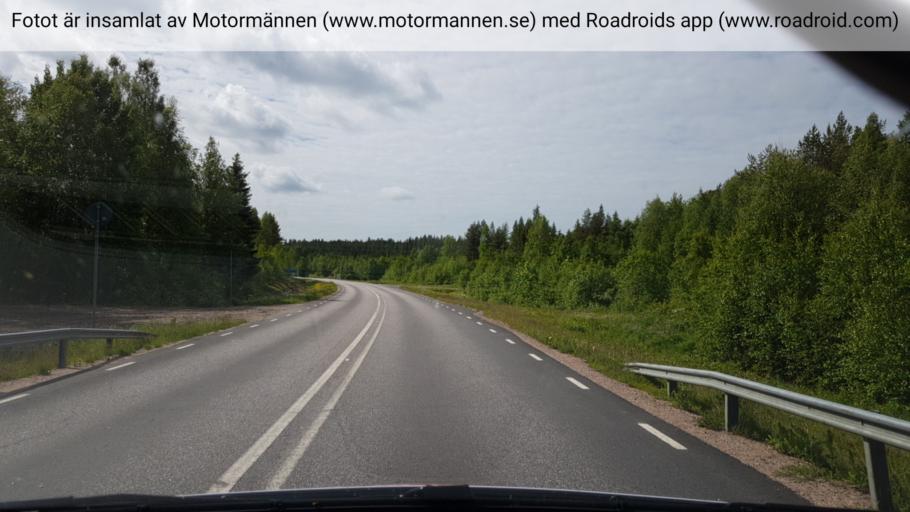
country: SE
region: Norrbotten
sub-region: Overtornea Kommun
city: OEvertornea
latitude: 66.5464
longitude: 23.7838
